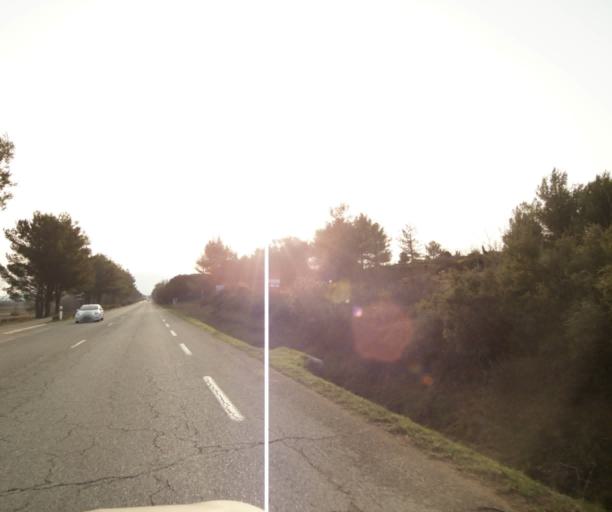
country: FR
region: Provence-Alpes-Cote d'Azur
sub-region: Departement des Bouches-du-Rhone
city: Peynier
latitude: 43.4601
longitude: 5.6419
